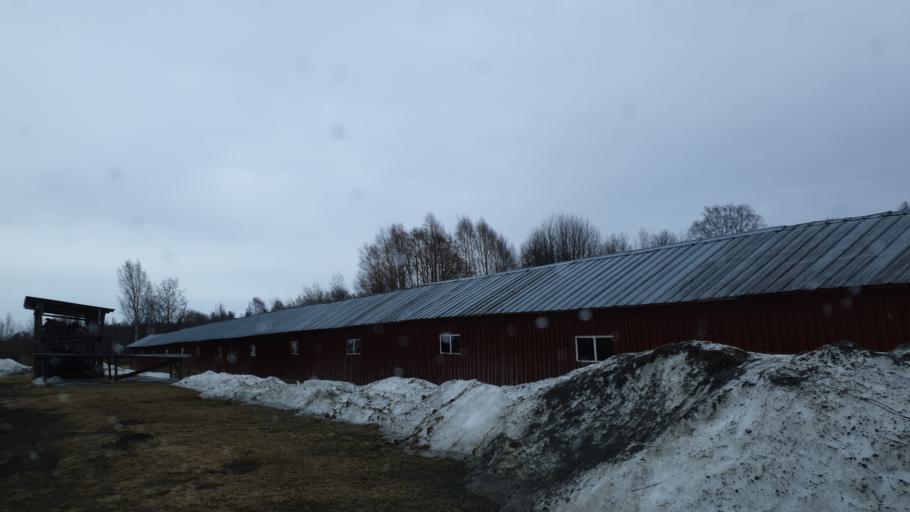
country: SE
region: Vaesterbotten
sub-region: Skelleftea Kommun
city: Kage
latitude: 64.8340
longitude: 20.9967
